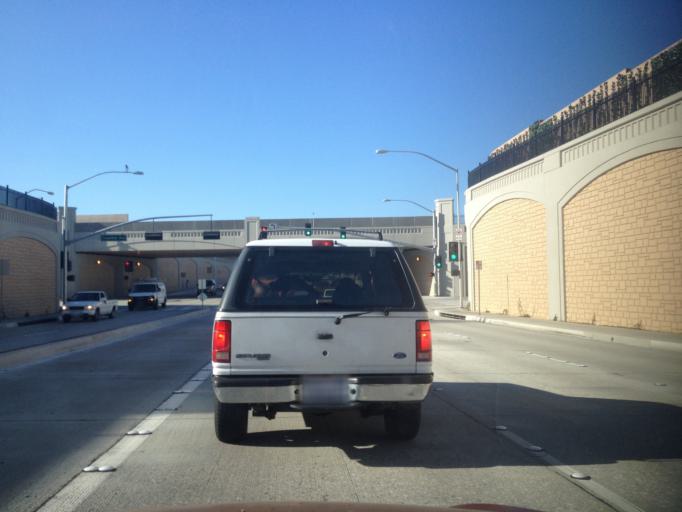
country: US
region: California
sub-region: Orange County
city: Placentia
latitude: 33.8684
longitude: -117.8631
